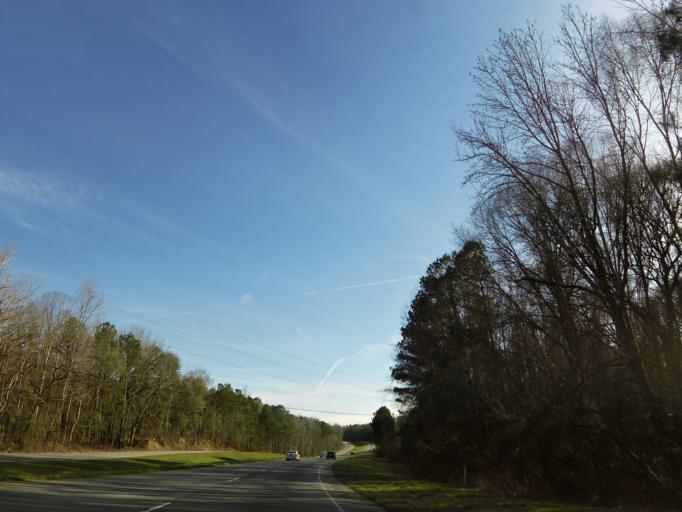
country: US
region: Georgia
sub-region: Chattahoochee County
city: Cusseta
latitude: 32.2519
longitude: -84.7210
